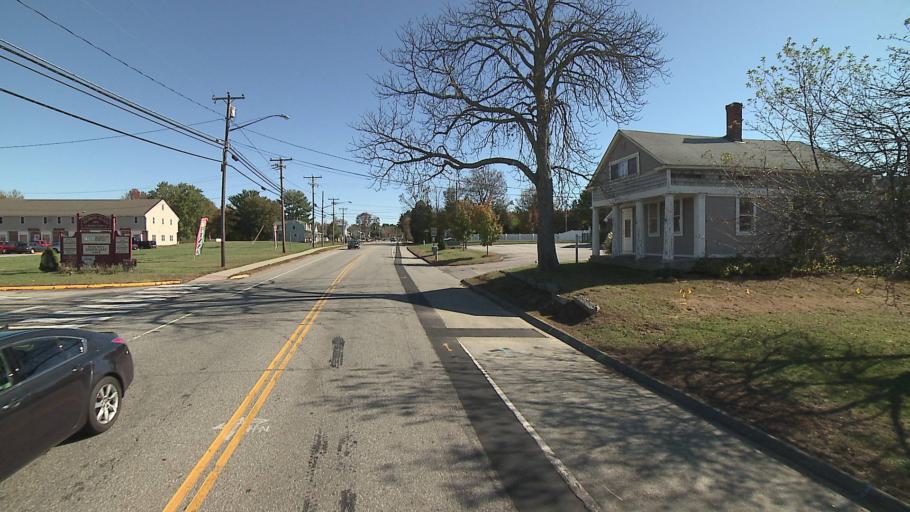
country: US
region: Connecticut
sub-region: Tolland County
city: Hebron
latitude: 41.6592
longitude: -72.3620
